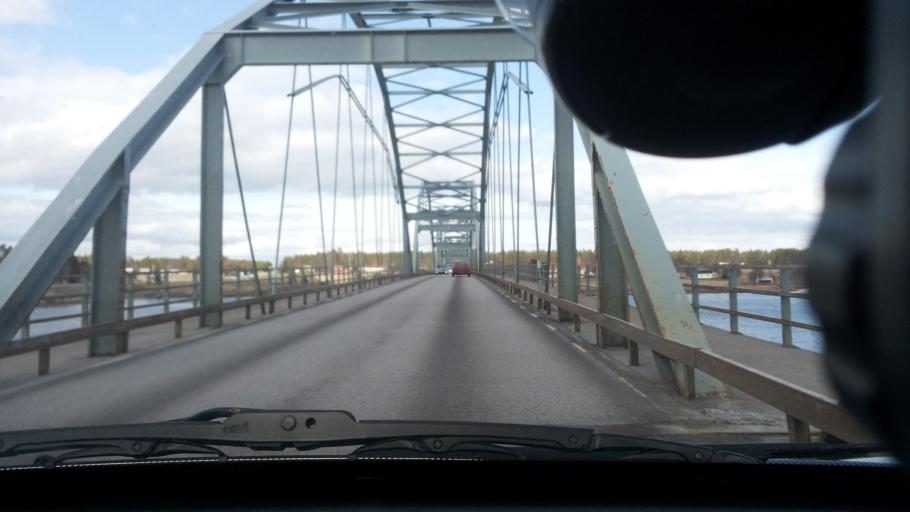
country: SE
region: Norrbotten
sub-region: Lulea Kommun
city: Gammelstad
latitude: 65.5878
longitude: 22.0304
